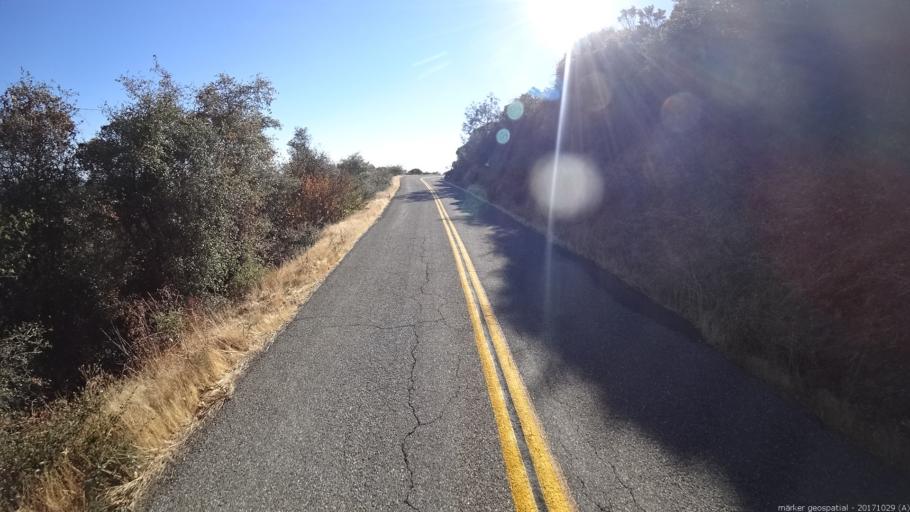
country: US
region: California
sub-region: Trinity County
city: Lewiston
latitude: 40.3674
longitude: -122.8481
